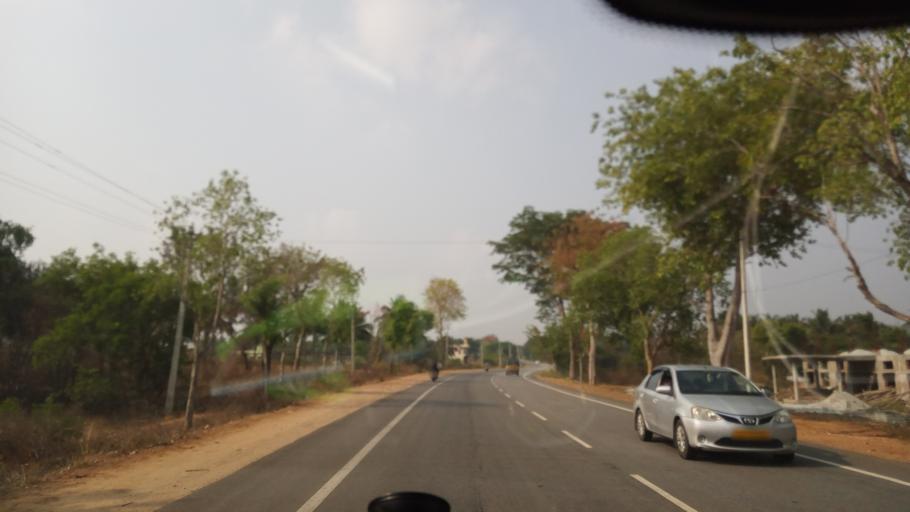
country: IN
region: Karnataka
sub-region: Mandya
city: Nagamangala
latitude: 12.8046
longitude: 76.7525
